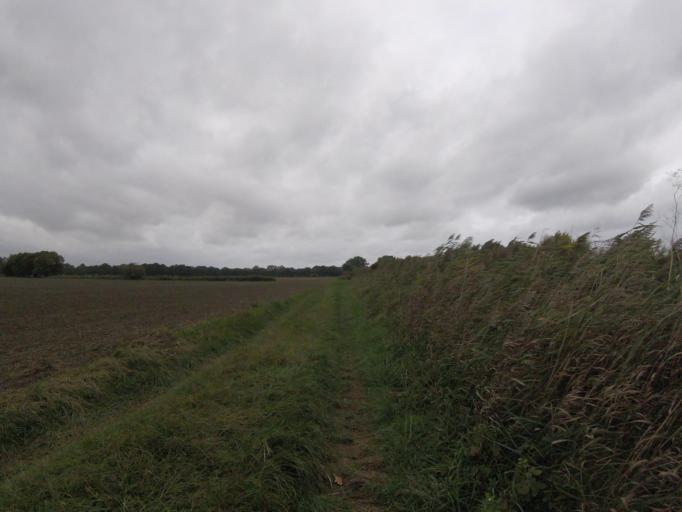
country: DE
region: Brandenburg
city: Mittenwalde
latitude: 52.2879
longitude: 13.5755
